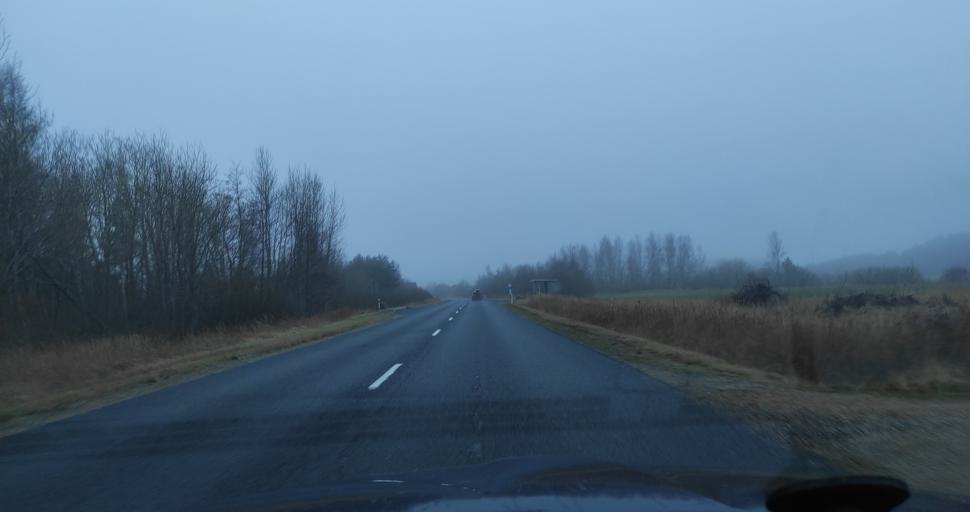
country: LV
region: Alsunga
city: Alsunga
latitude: 57.1157
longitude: 21.4236
